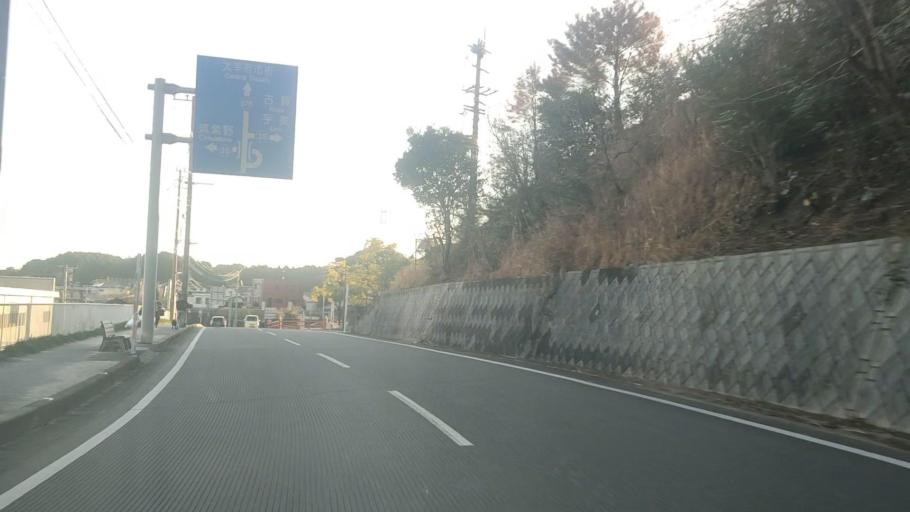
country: JP
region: Fukuoka
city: Dazaifu
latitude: 33.5273
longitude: 130.5437
